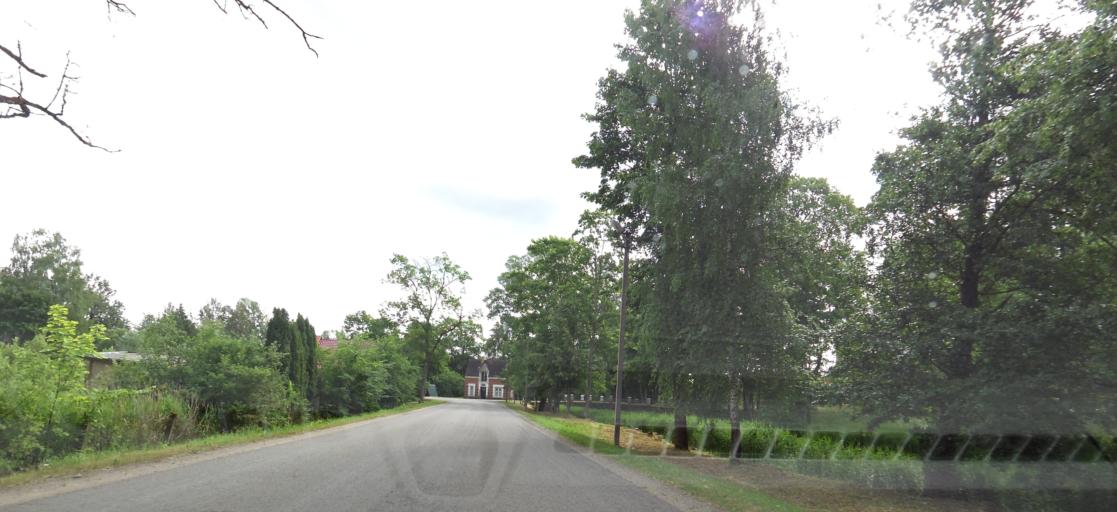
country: LT
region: Panevezys
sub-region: Birzai
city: Birzai
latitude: 56.2222
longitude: 24.7683
